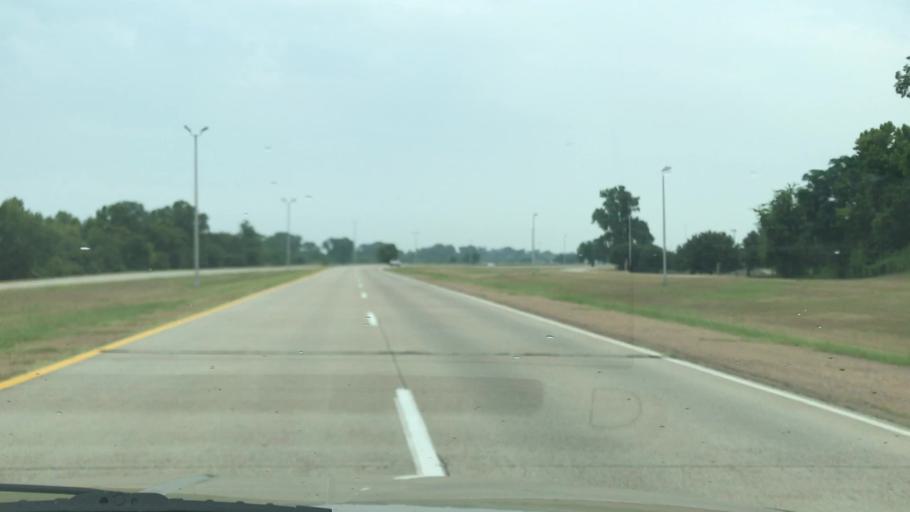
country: US
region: Louisiana
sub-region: Bossier Parish
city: Bossier City
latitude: 32.4863
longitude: -93.6959
